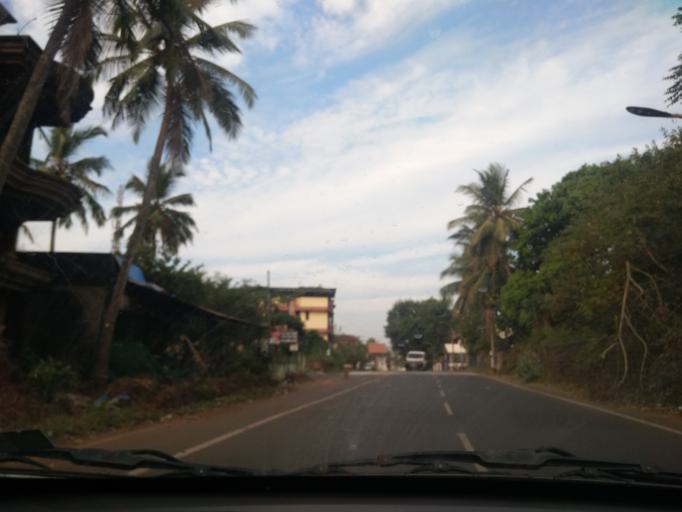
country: IN
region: Goa
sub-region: South Goa
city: Raia
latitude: 15.2900
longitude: 73.9689
